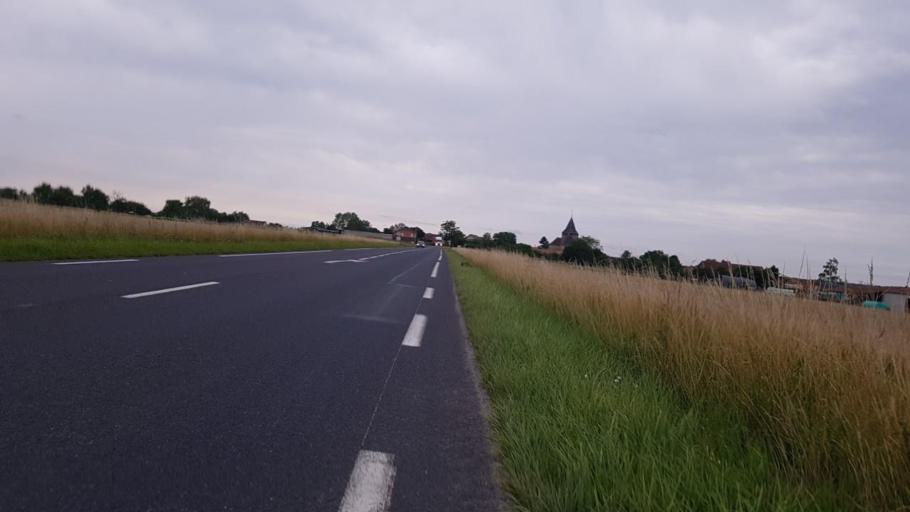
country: FR
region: Champagne-Ardenne
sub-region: Departement de la Marne
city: Pargny-sur-Saulx
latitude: 48.7638
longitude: 4.8127
